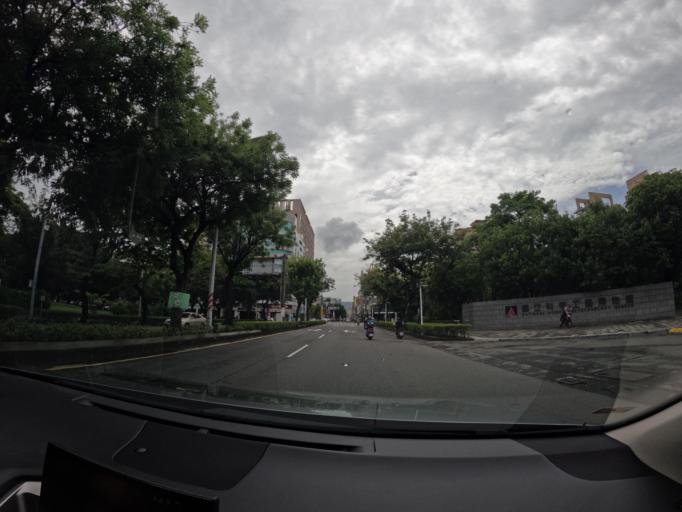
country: TW
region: Kaohsiung
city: Kaohsiung
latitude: 22.6398
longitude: 120.3218
